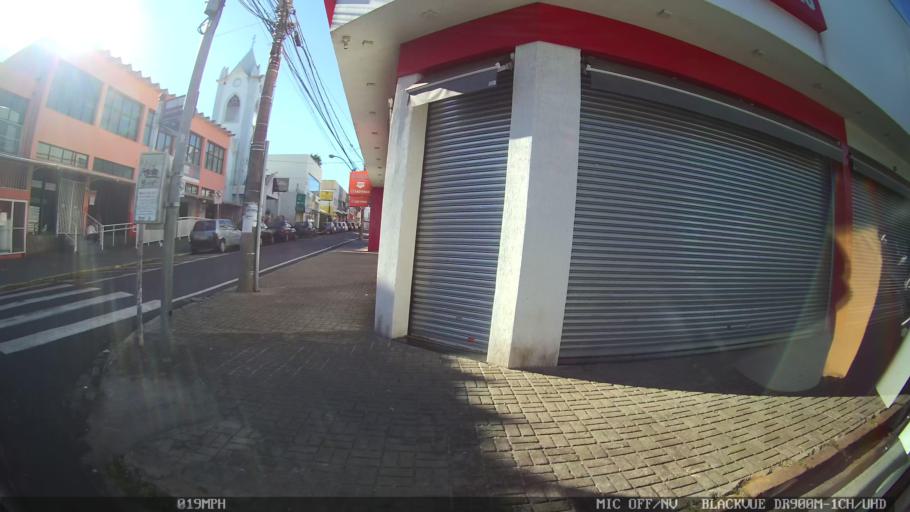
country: BR
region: Sao Paulo
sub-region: Franca
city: Franca
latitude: -20.5359
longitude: -47.4026
